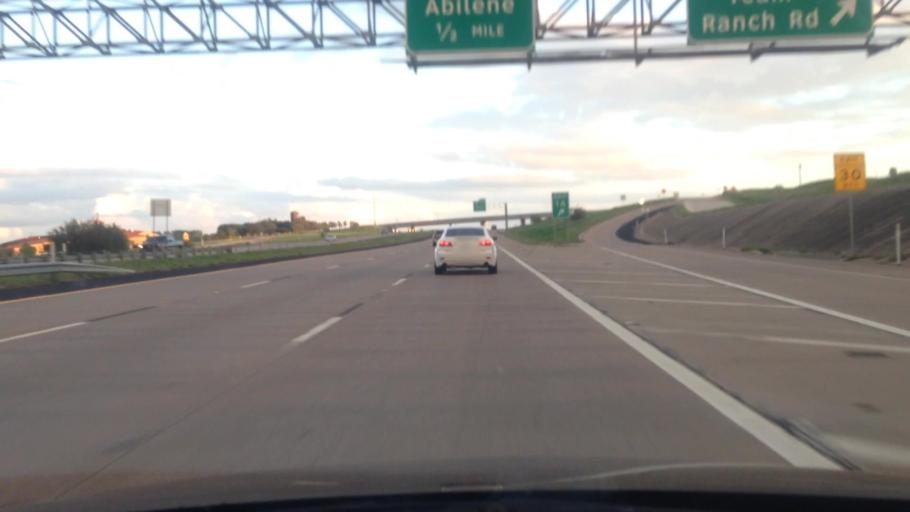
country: US
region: Texas
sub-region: Tarrant County
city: Benbrook
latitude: 32.7072
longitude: -97.4752
